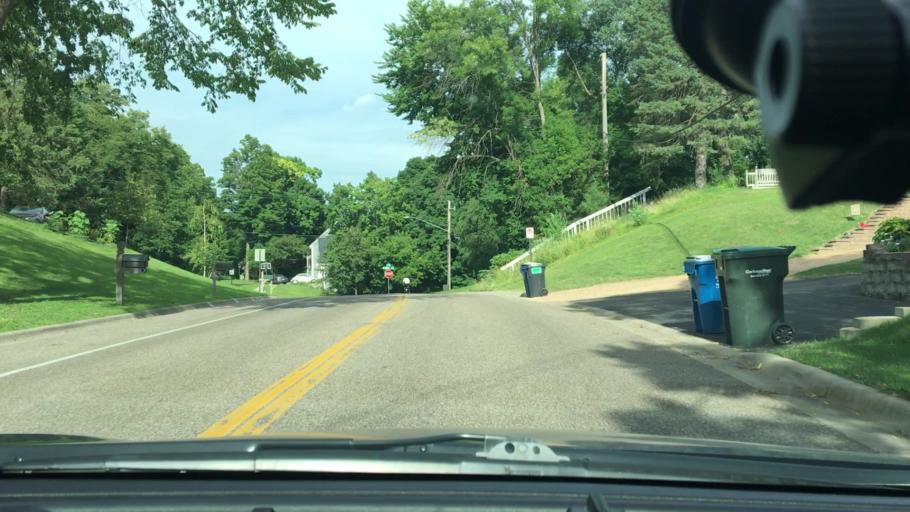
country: US
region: Minnesota
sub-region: Hennepin County
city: Plymouth
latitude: 45.0072
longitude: -93.4333
